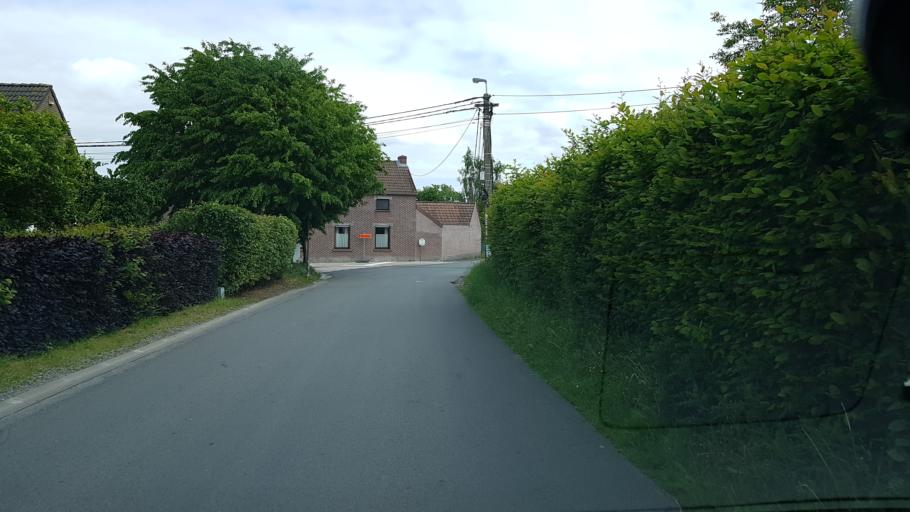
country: BE
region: Wallonia
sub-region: Province du Brabant Wallon
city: Tubize
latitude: 50.6342
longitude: 4.1981
